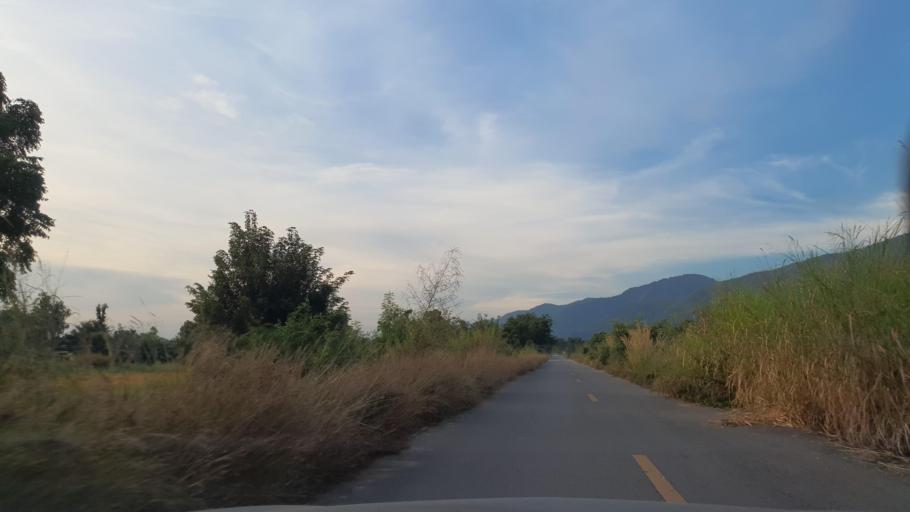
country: TH
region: Uthai Thani
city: Sawang Arom
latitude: 15.7023
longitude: 99.9610
